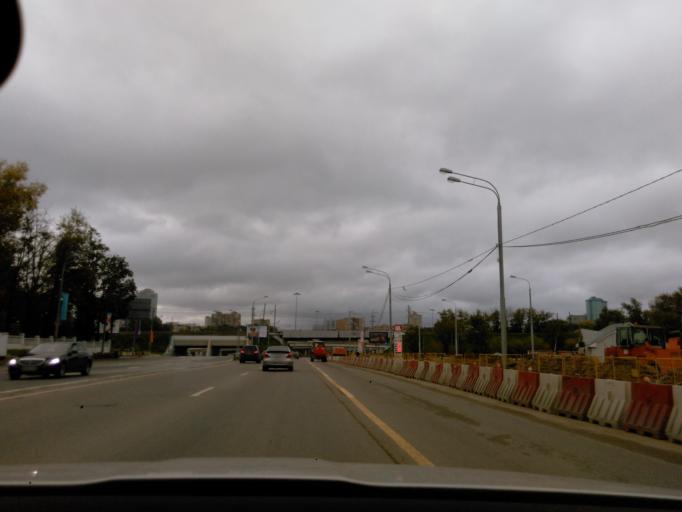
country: RU
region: Moscow
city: Pokrovskoye-Streshnevo
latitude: 55.8217
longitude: 37.4446
